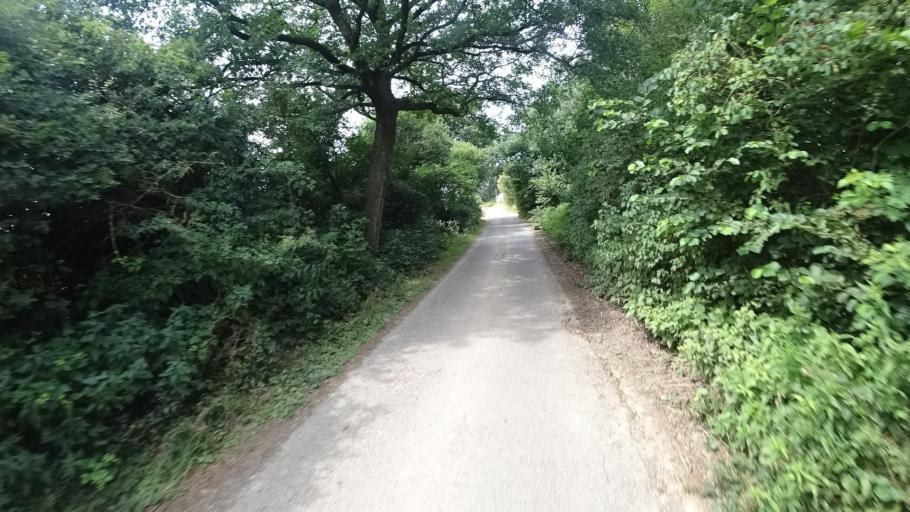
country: DE
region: Rheinland-Pfalz
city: Berzhausen
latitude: 50.6708
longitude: 7.5710
